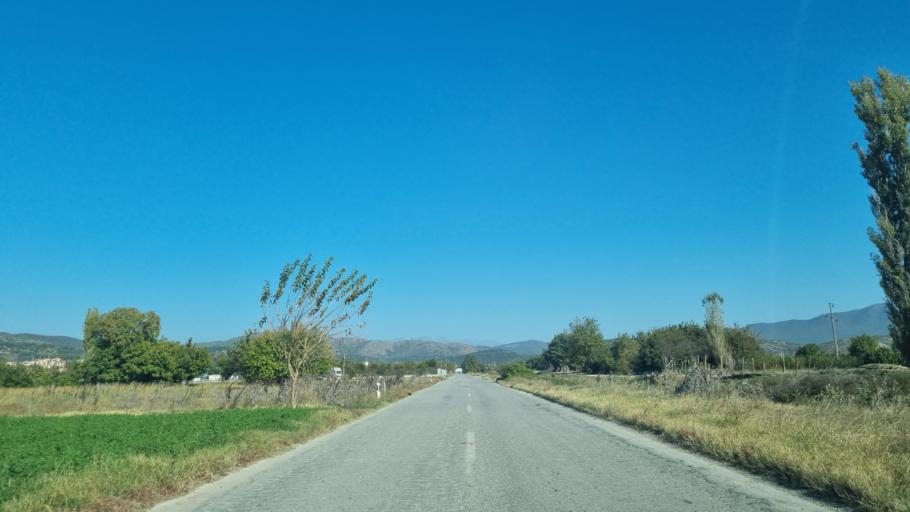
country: MK
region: Bogdanci
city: Bogdanci
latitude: 41.1917
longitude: 22.5661
